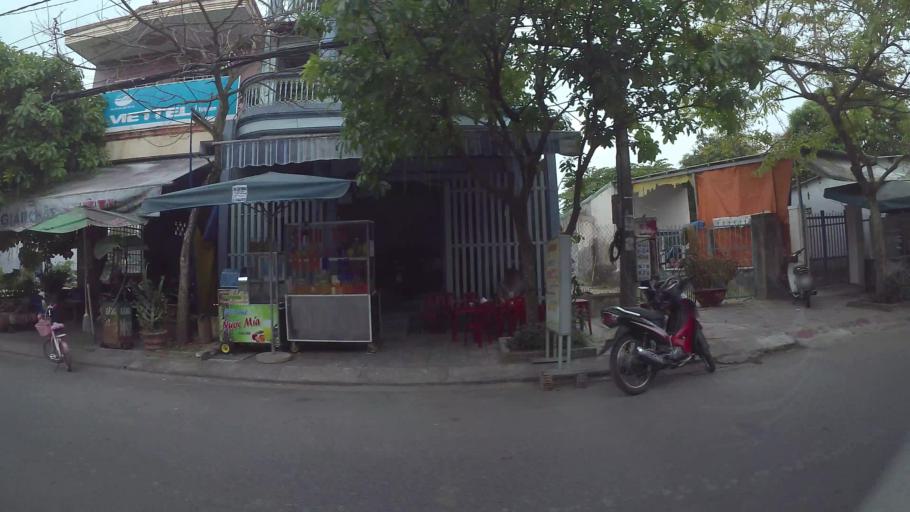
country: VN
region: Da Nang
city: Lien Chieu
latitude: 16.0608
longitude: 108.1672
